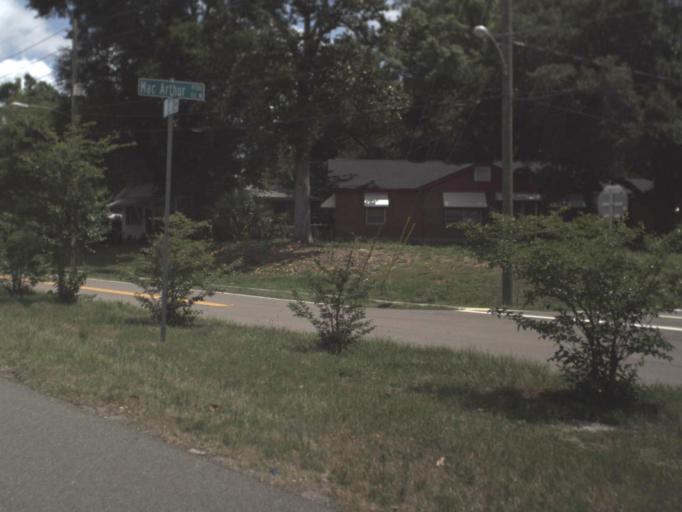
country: US
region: Florida
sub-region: Duval County
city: Jacksonville
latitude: 30.2938
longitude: -81.5586
